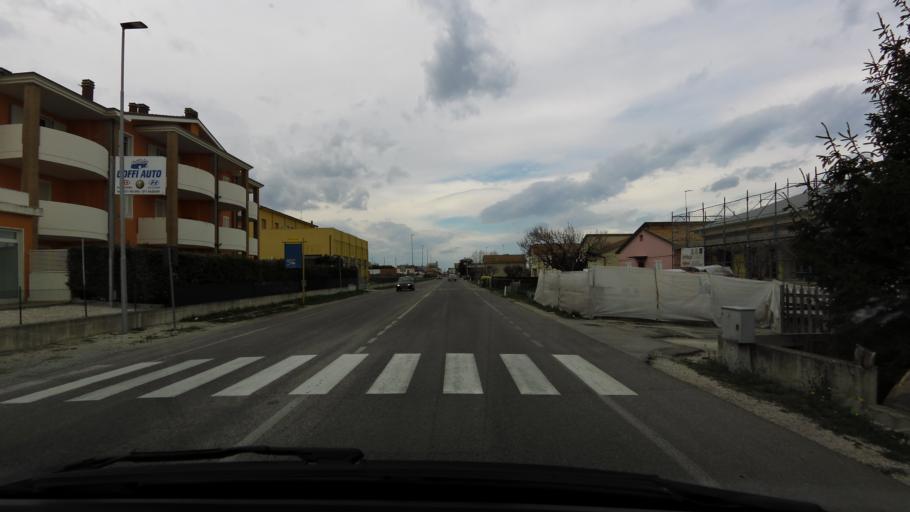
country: IT
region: The Marches
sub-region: Provincia di Pesaro e Urbino
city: Marotta
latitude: 43.7554
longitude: 13.1595
